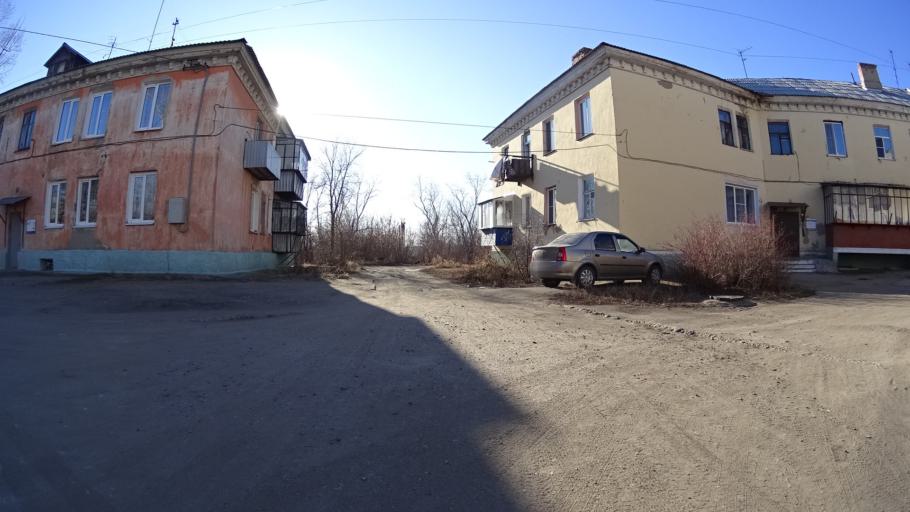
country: RU
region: Chelyabinsk
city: Troitsk
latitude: 54.0433
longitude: 61.6277
